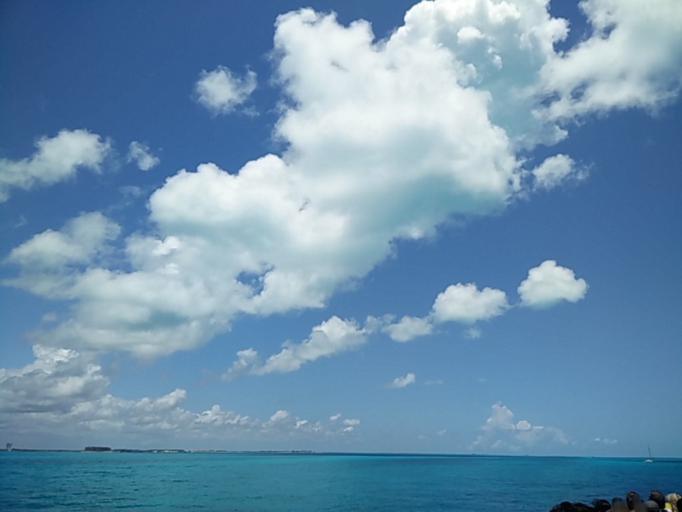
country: MX
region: Quintana Roo
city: Isla Mujeres
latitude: 21.2098
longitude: -86.7591
